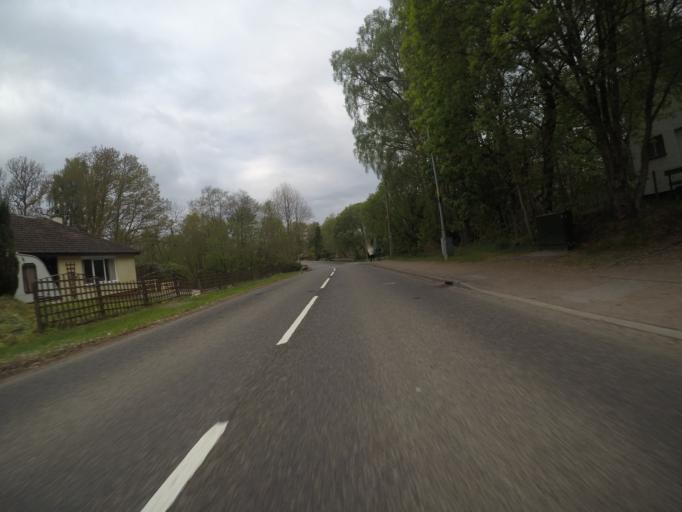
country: GB
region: Scotland
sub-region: Highland
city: Spean Bridge
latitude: 56.8939
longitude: -4.9150
